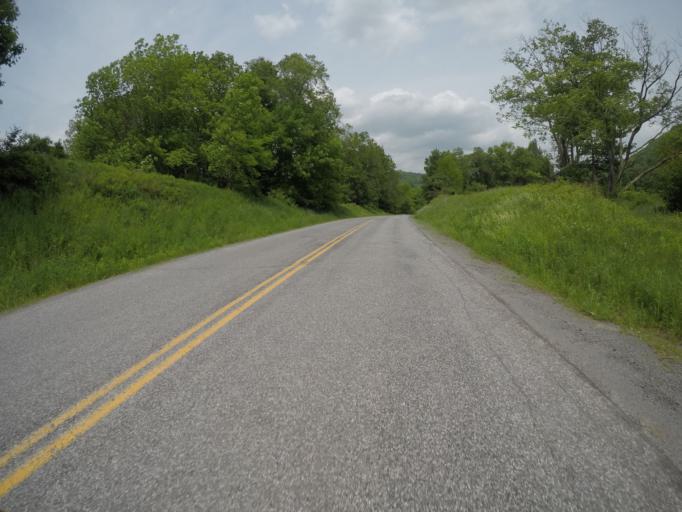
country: US
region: New York
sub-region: Delaware County
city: Stamford
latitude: 42.1639
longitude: -74.6842
